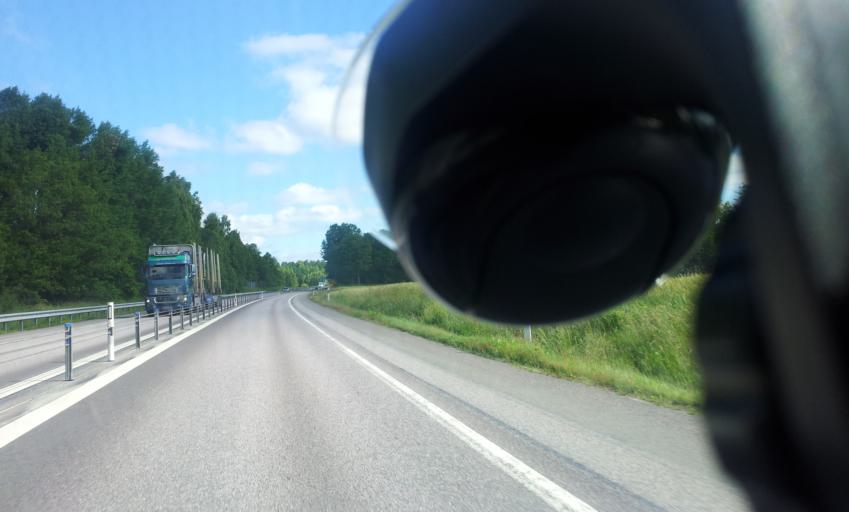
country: SE
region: Kalmar
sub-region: Monsteras Kommun
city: Timmernabben
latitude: 56.9603
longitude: 16.3909
